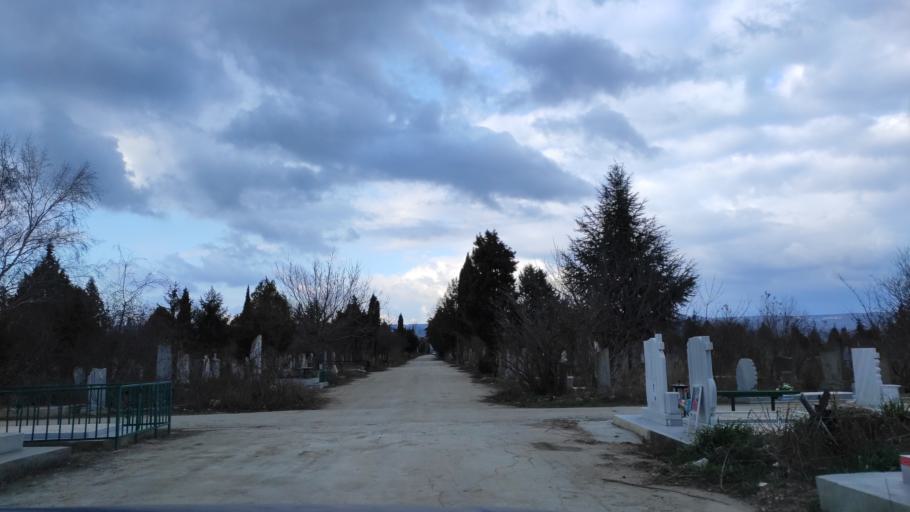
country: BG
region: Varna
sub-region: Obshtina Aksakovo
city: Aksakovo
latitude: 43.2177
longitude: 27.8089
